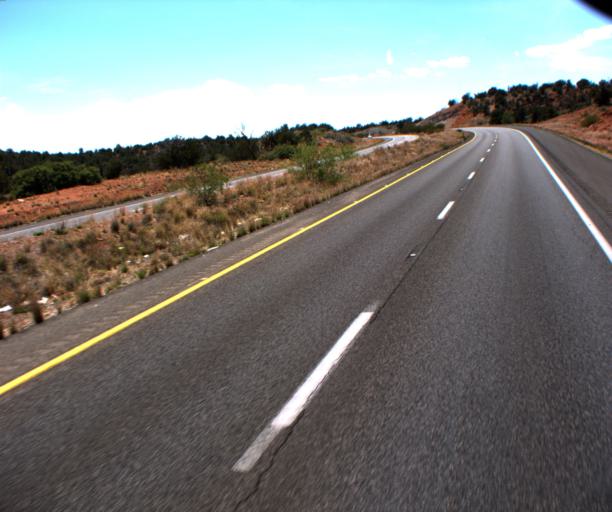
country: US
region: Arizona
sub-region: Yavapai County
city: West Sedona
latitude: 34.8387
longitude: -111.8835
